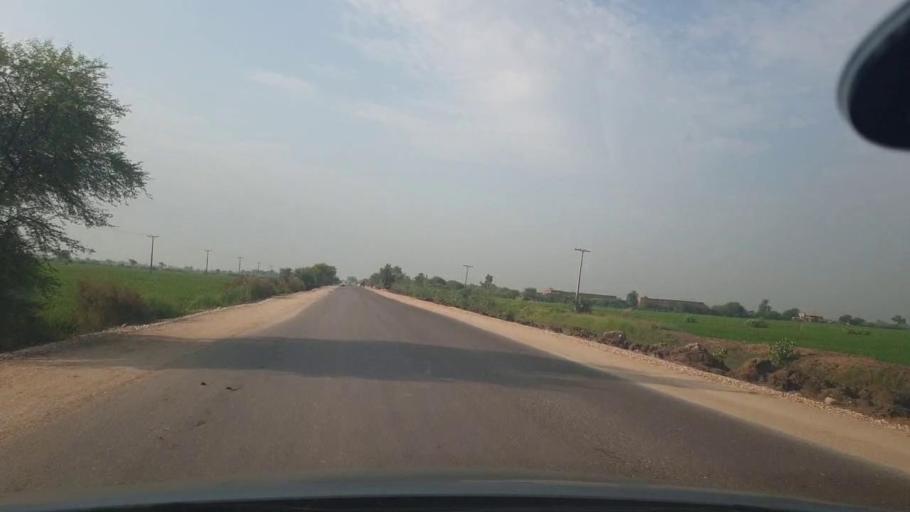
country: PK
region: Sindh
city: Jacobabad
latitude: 28.2097
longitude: 68.3684
